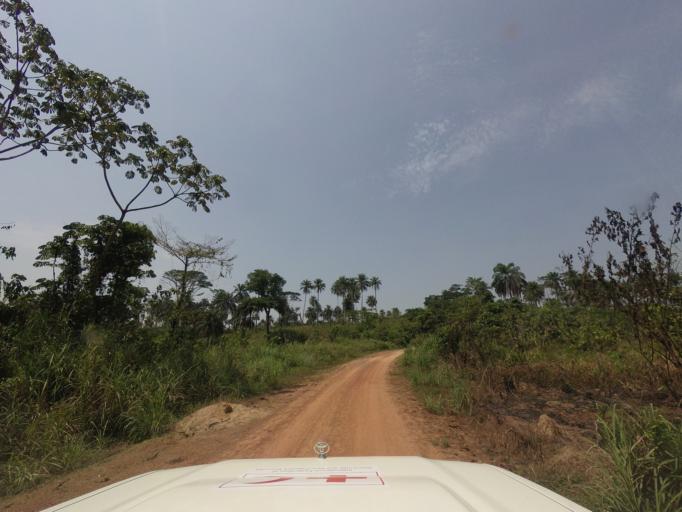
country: LR
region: Lofa
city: Voinjama
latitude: 8.4731
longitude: -9.6633
